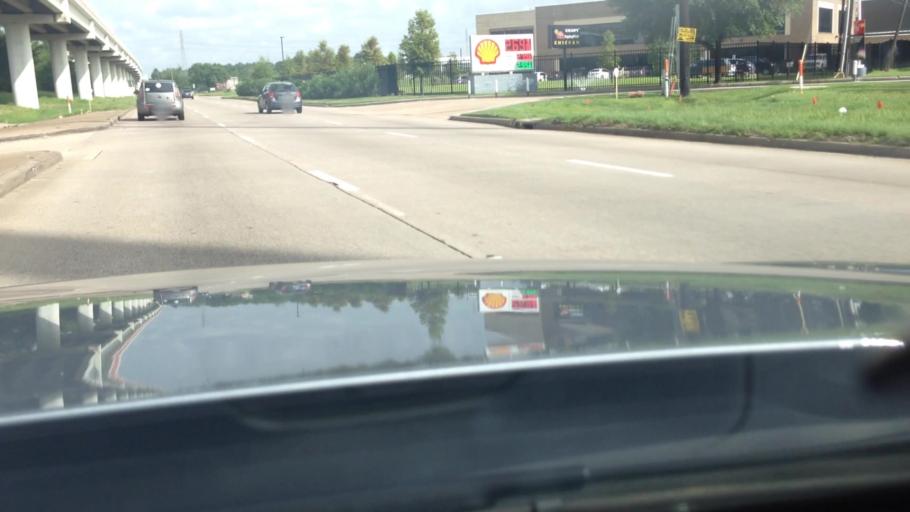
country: US
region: Texas
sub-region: Harris County
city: Hudson
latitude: 29.9376
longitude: -95.5164
